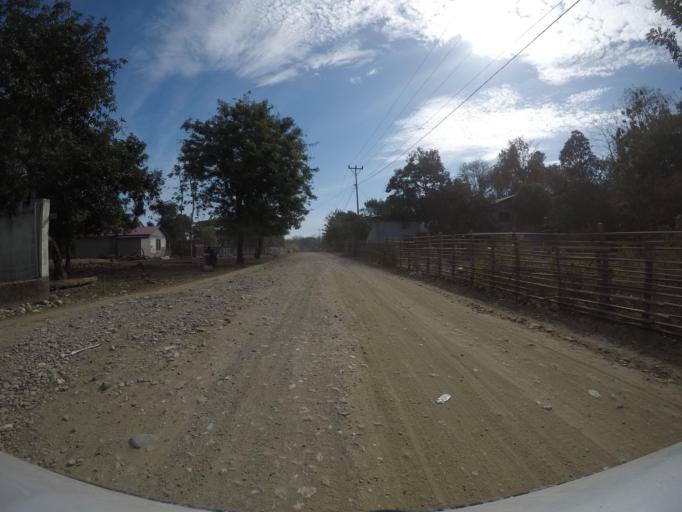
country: TL
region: Bobonaro
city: Maliana
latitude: -8.8821
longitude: 125.2099
